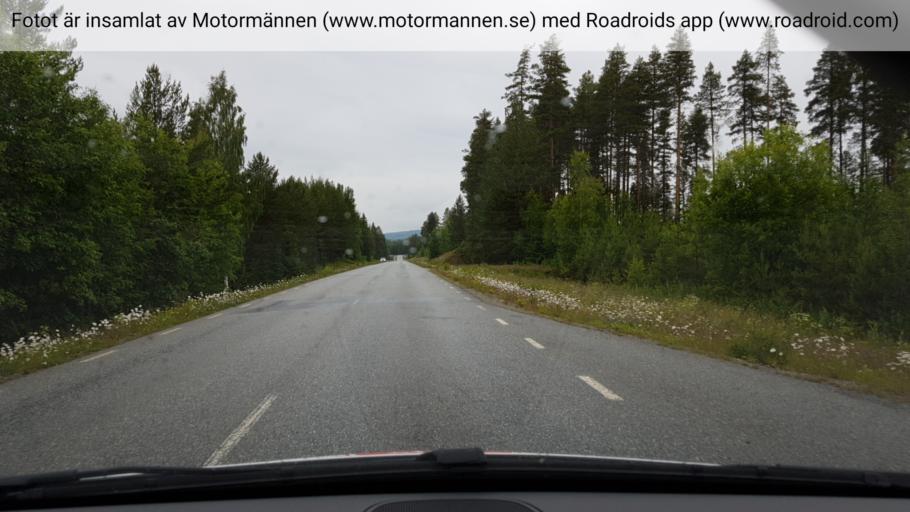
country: SE
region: Vaesterbotten
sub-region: Dorotea Kommun
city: Dorotea
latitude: 64.1487
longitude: 16.0538
